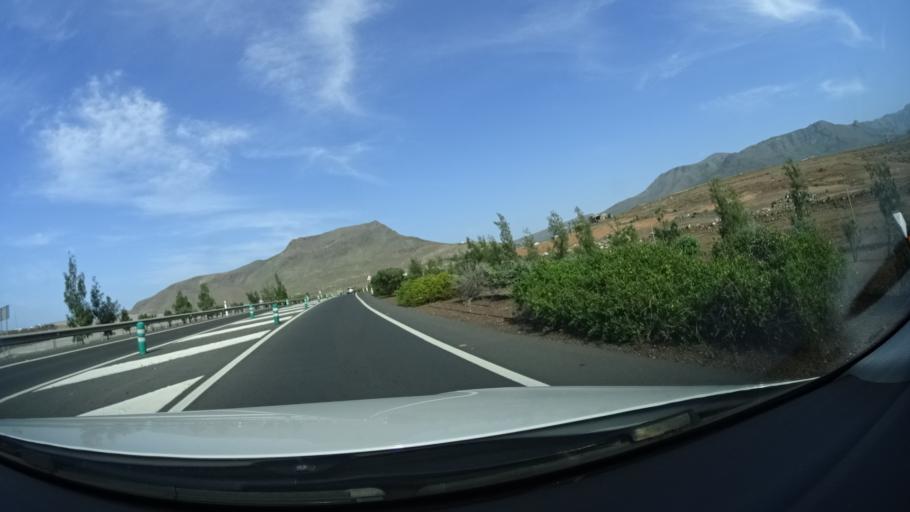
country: ES
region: Canary Islands
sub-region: Provincia de Las Palmas
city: Agaete
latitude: 28.1126
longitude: -15.6970
